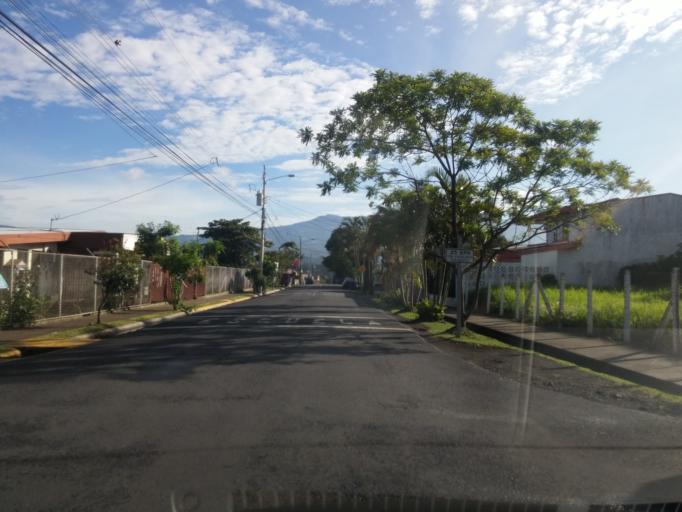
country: CR
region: Heredia
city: Llorente
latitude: 10.0025
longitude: -84.1539
